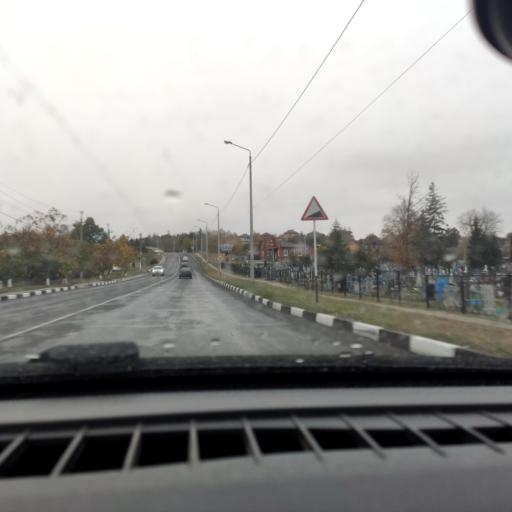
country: RU
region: Belgorod
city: Alekseyevka
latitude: 50.6414
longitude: 38.6926
